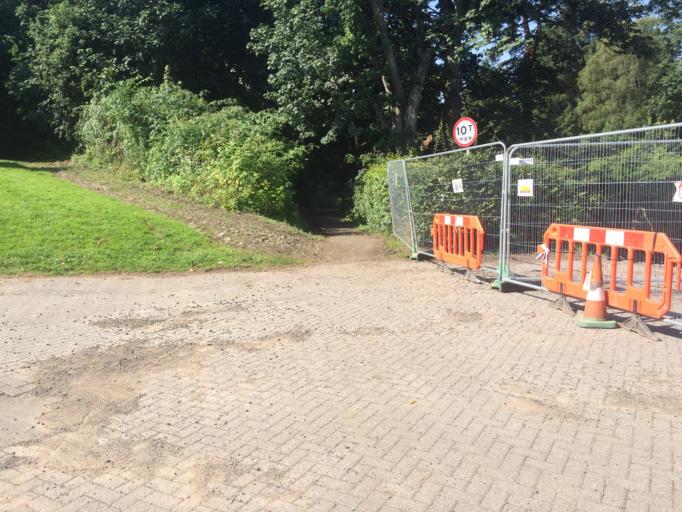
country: GB
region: Scotland
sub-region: Dundee City
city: Dundee
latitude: 56.4856
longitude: -2.9589
